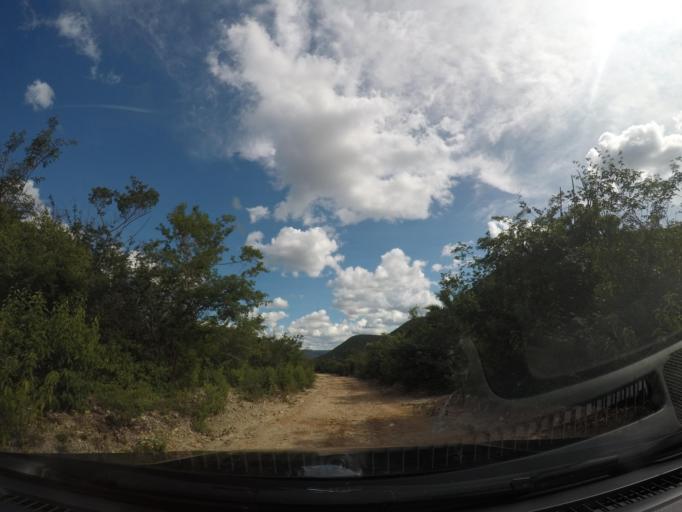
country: BR
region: Bahia
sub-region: Barra Da Estiva
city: Barra da Estiva
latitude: -13.1500
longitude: -41.5961
